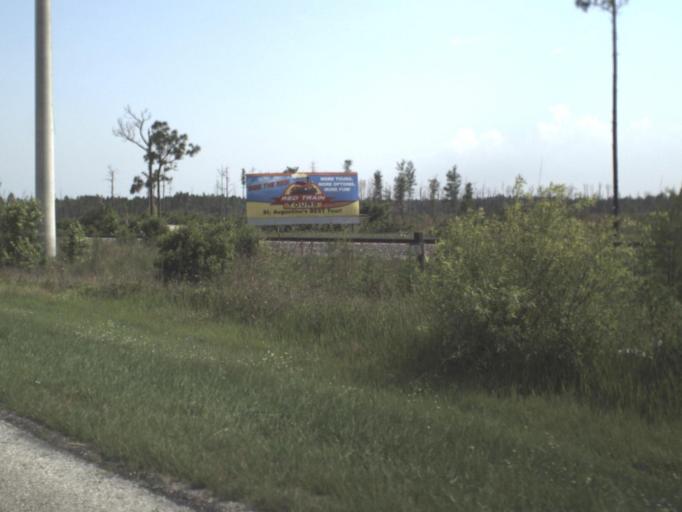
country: US
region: Florida
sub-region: Saint Johns County
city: Palm Valley
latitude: 30.0421
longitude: -81.4189
